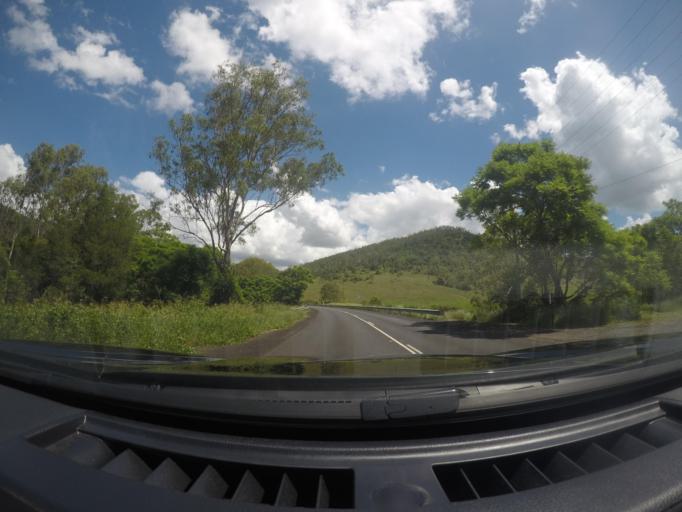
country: AU
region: Queensland
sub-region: Moreton Bay
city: Woodford
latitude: -27.1247
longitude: 152.5506
